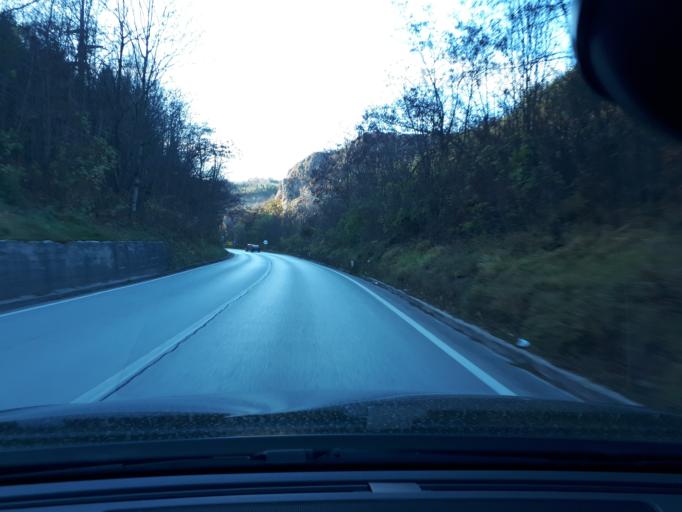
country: BA
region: Republika Srpska
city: Pale
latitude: 43.8522
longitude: 18.5324
